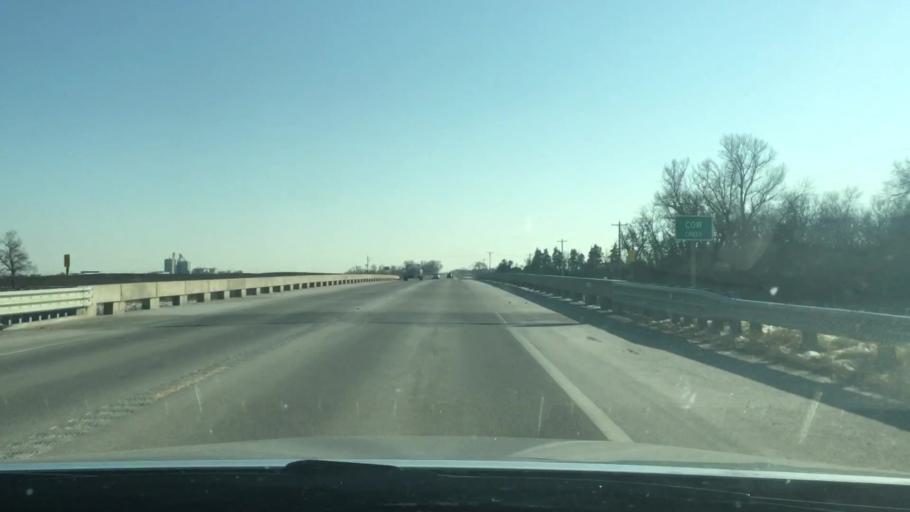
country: US
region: Kansas
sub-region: Rice County
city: Lyons
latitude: 38.3074
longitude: -98.2019
